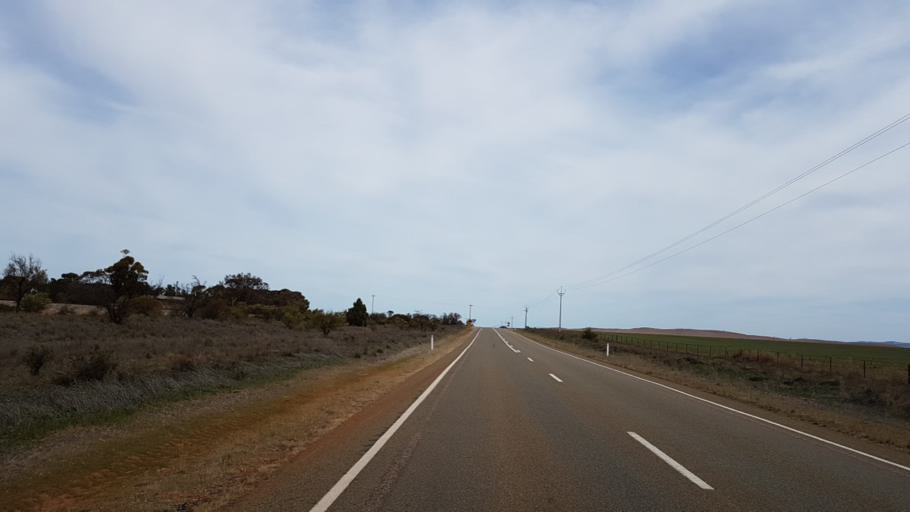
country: AU
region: South Australia
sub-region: Peterborough
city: Peterborough
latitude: -32.9995
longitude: 138.7794
